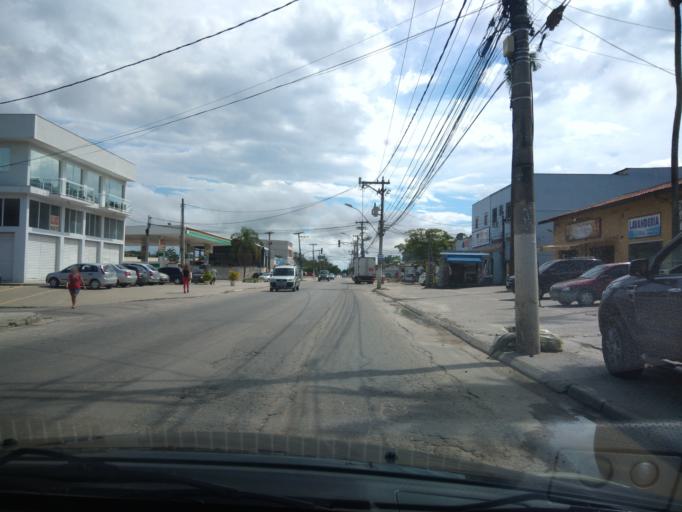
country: BR
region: Rio de Janeiro
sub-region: Niteroi
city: Niteroi
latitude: -22.9274
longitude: -43.0121
